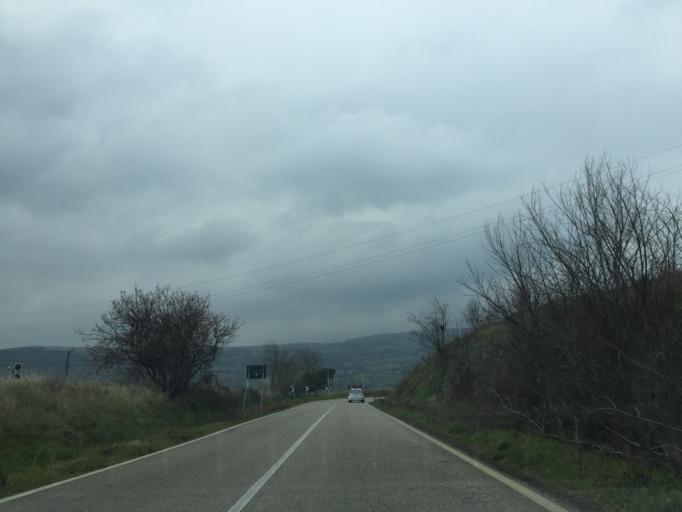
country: IT
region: Apulia
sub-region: Provincia di Foggia
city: Bovino
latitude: 41.2842
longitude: 15.3790
